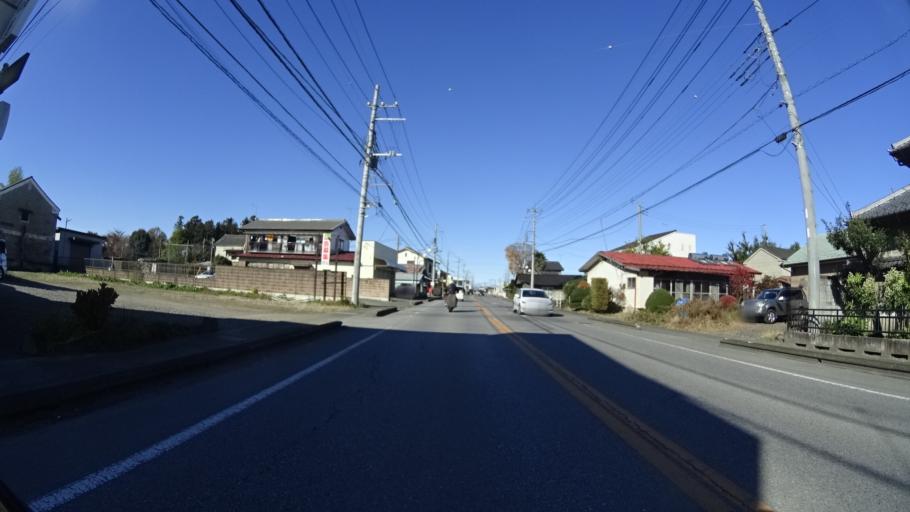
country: JP
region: Tochigi
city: Kanuma
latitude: 36.5214
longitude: 139.7507
